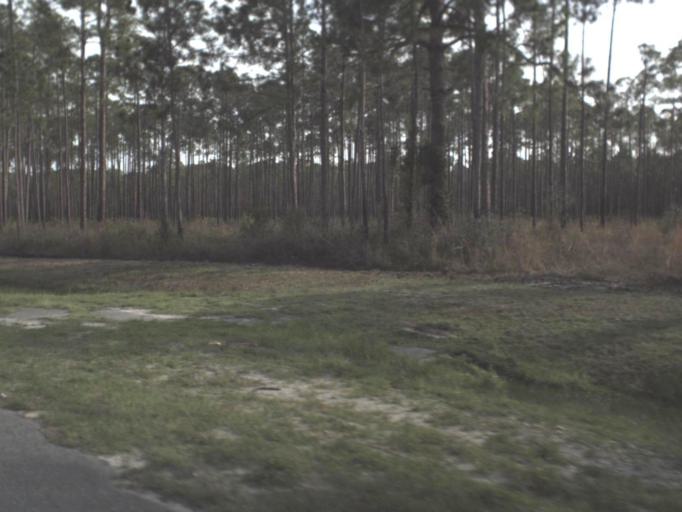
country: US
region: Florida
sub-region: Bay County
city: Mexico Beach
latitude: 30.0008
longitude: -85.5006
